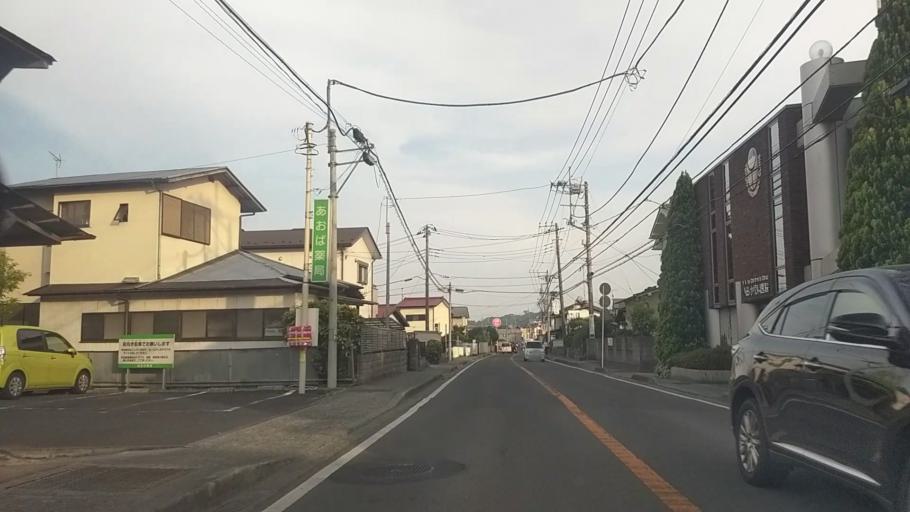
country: JP
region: Kanagawa
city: Odawara
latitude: 35.2933
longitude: 139.1325
